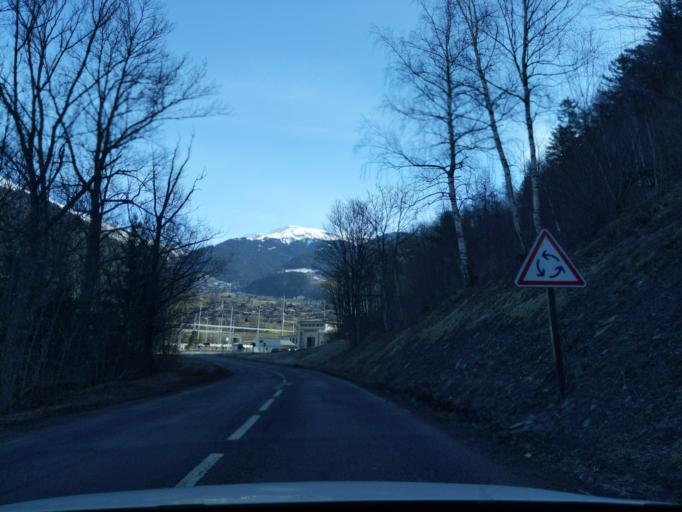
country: FR
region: Rhone-Alpes
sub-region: Departement de la Savoie
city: Seez
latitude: 45.6173
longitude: 6.7851
